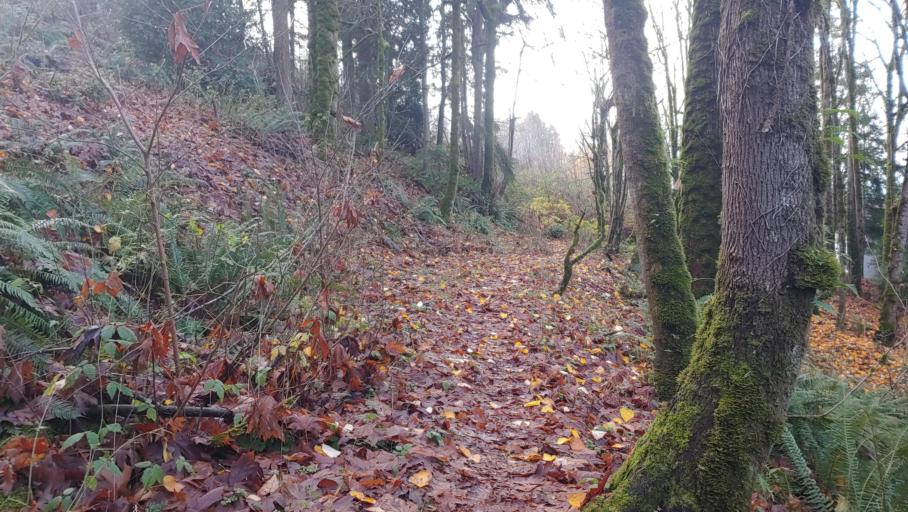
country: US
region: Washington
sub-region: King County
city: Eastgate
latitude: 47.5695
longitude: -122.1514
